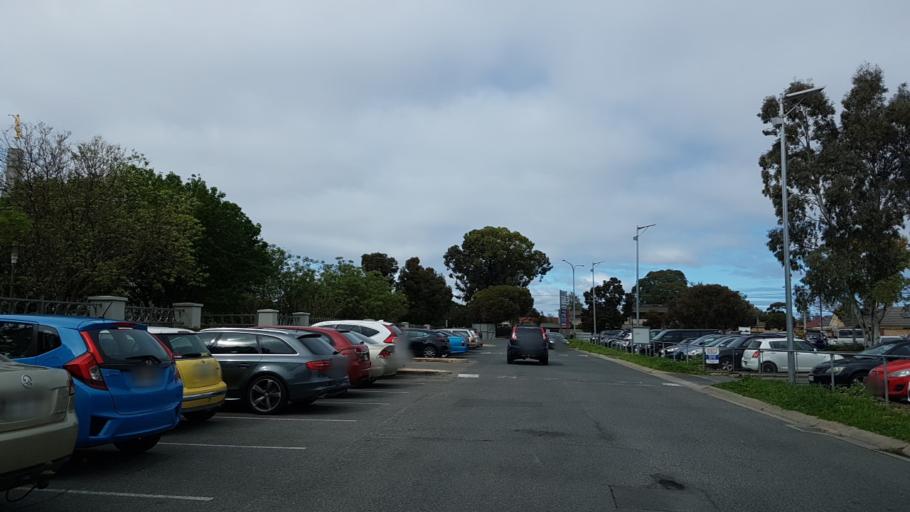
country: AU
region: South Australia
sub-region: Norwood Payneham St Peters
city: Marden
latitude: -34.8916
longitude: 138.6348
